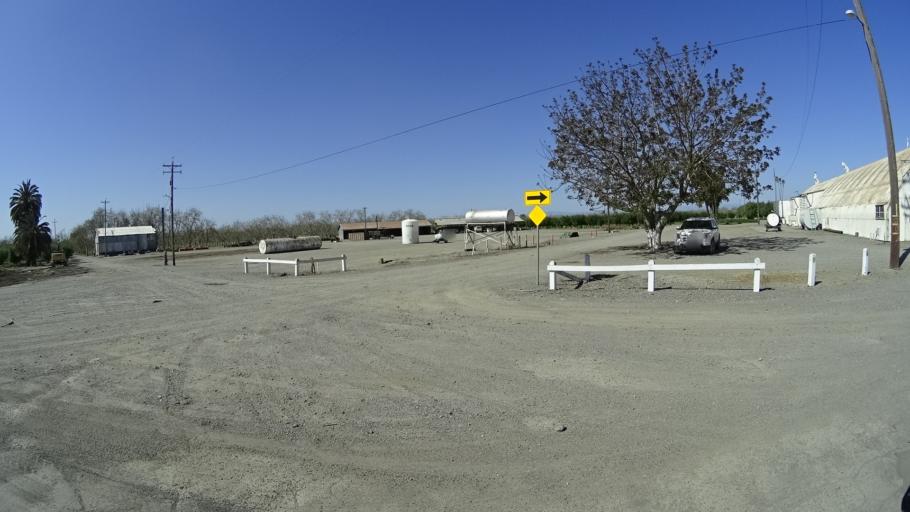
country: US
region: California
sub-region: Glenn County
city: Hamilton City
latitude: 39.7377
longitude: -122.0572
